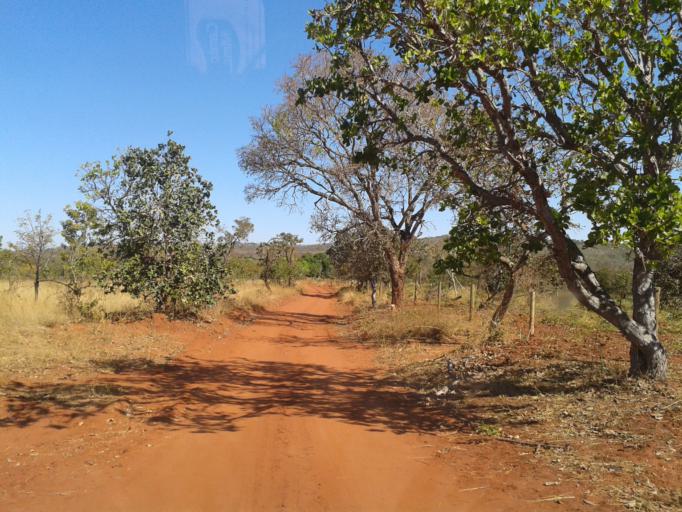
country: BR
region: Minas Gerais
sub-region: Ituiutaba
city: Ituiutaba
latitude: -19.0816
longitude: -49.3374
